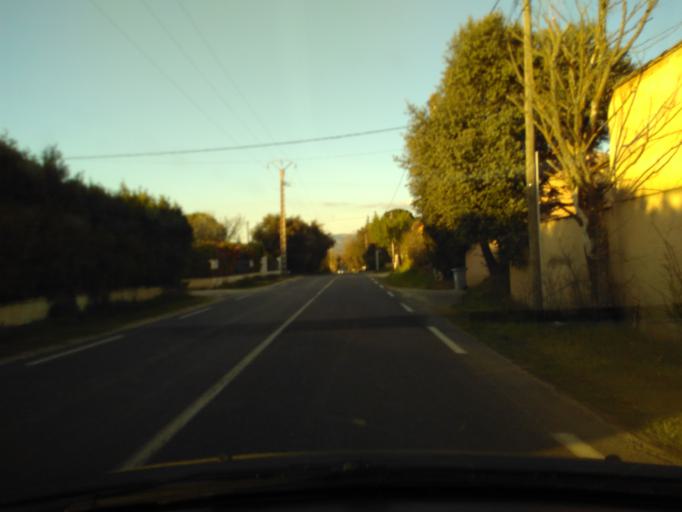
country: FR
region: Provence-Alpes-Cote d'Azur
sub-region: Departement du Vaucluse
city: Carpentras
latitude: 44.0706
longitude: 5.0723
